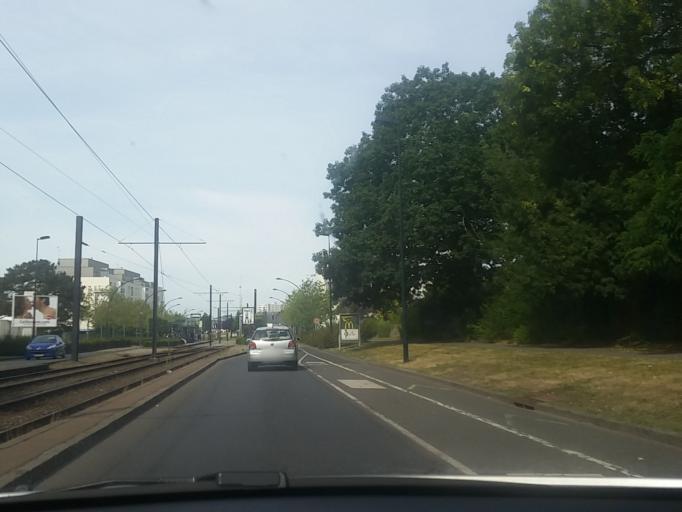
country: FR
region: Pays de la Loire
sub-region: Departement de la Loire-Atlantique
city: Nantes
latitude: 47.2099
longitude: -1.5939
